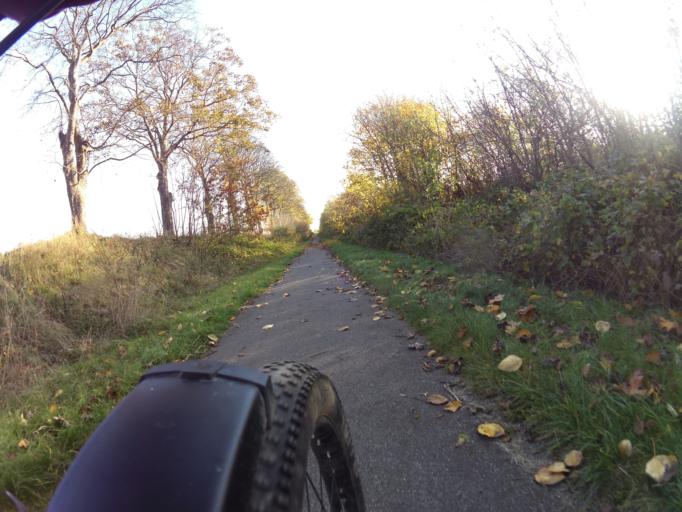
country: PL
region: Pomeranian Voivodeship
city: Strzelno
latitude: 54.7660
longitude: 18.2457
